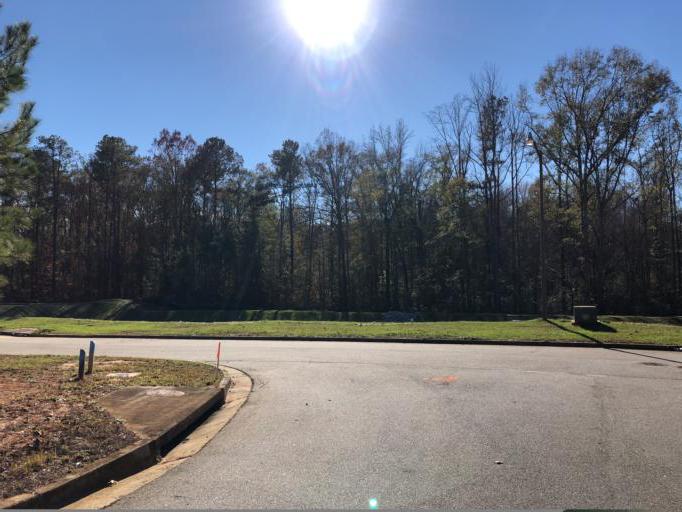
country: US
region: Georgia
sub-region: Spalding County
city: Experiment
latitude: 33.2862
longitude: -84.3022
